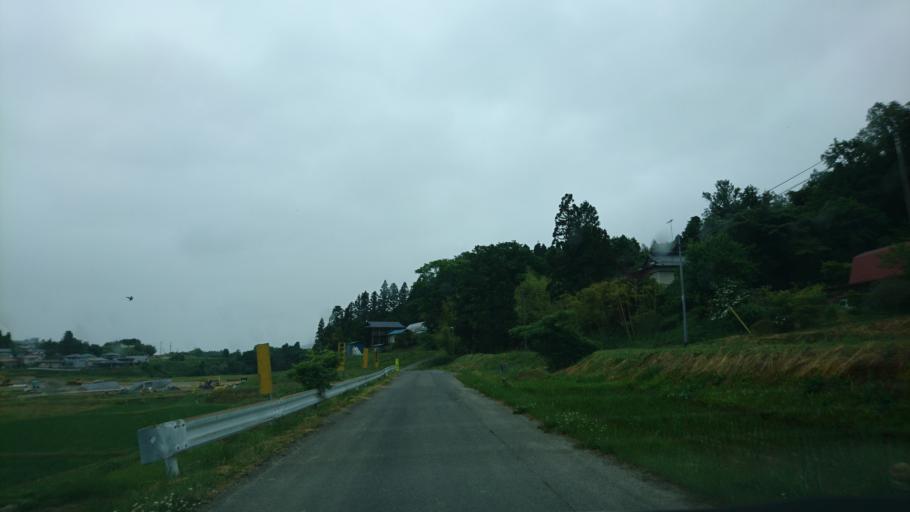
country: JP
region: Iwate
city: Ichinoseki
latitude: 38.9310
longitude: 141.1752
